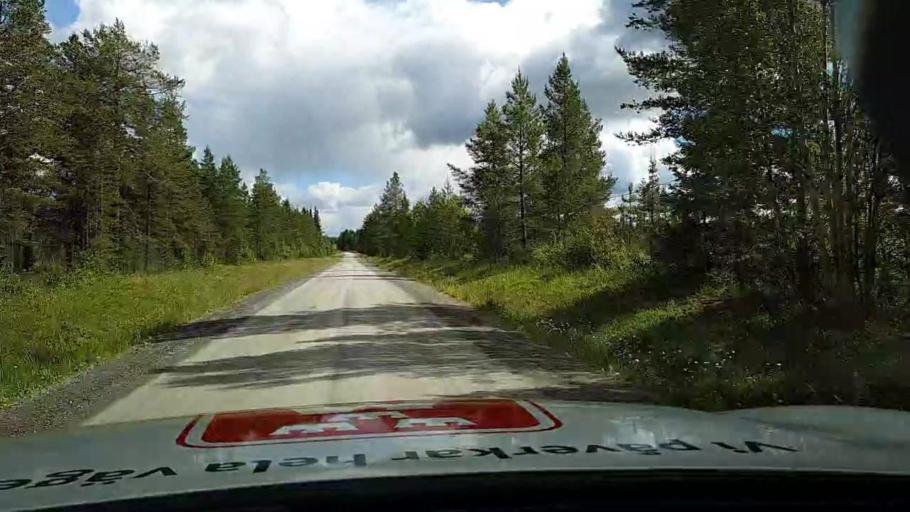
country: SE
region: Jaemtland
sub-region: Krokoms Kommun
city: Valla
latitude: 63.7069
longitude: 13.5904
